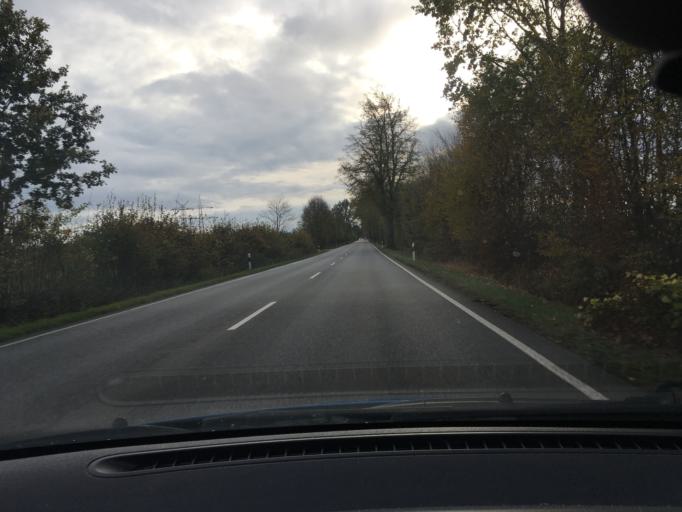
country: DE
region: Schleswig-Holstein
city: Kankelau
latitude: 53.5566
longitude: 10.5522
